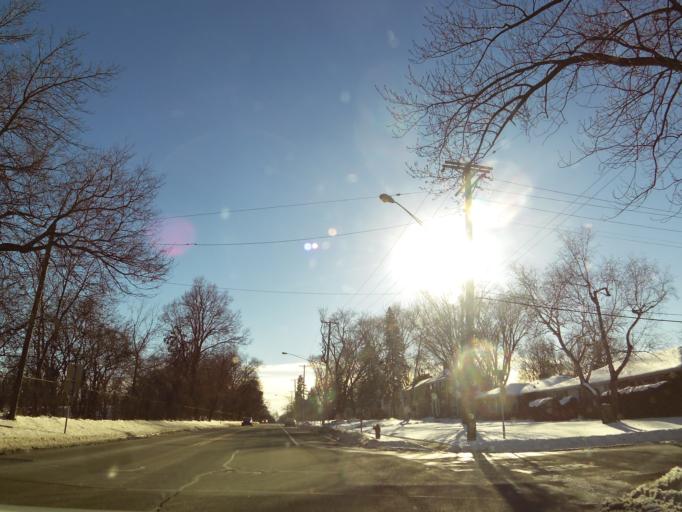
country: US
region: Minnesota
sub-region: Hennepin County
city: Saint Louis Park
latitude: 44.9361
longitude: -93.3291
